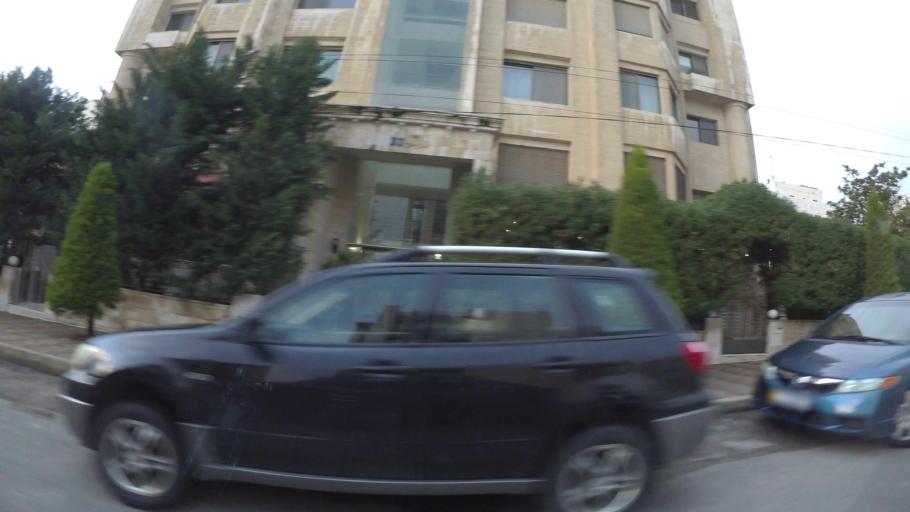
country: JO
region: Amman
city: Amman
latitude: 31.9623
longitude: 35.8861
